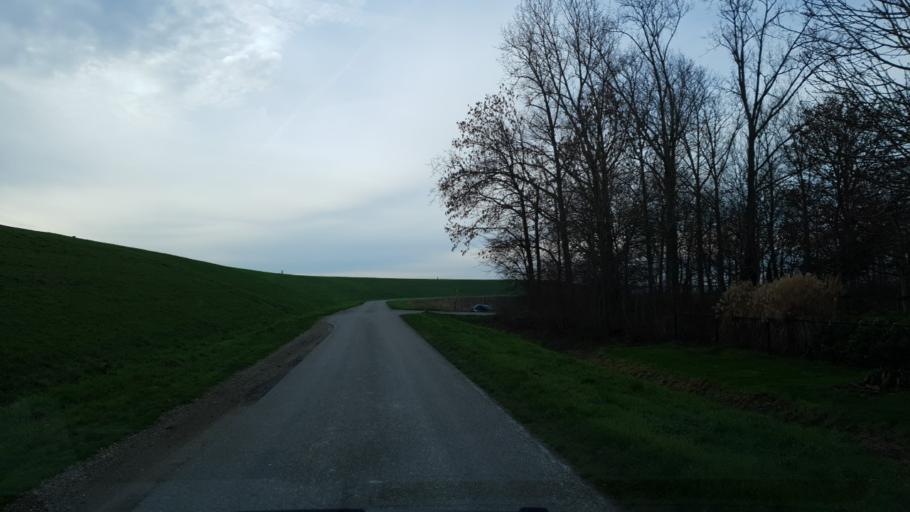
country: NL
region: North Brabant
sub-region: Gemeente Woensdrecht
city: Woensdrecht
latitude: 51.4006
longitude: 4.1670
